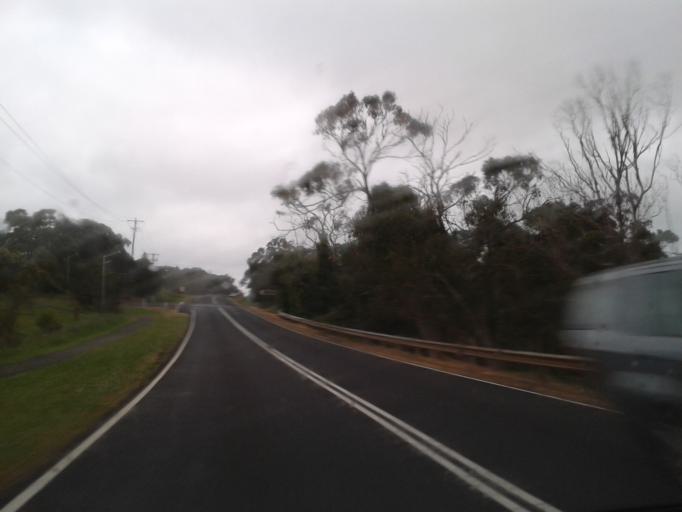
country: AU
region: Victoria
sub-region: Glenelg
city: Portland
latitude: -38.3407
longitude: 141.5841
